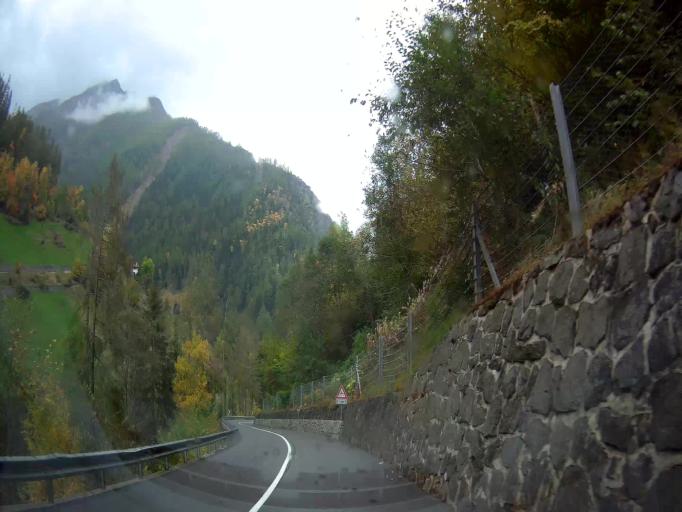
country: IT
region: Trentino-Alto Adige
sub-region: Bolzano
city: Certosa
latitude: 46.7052
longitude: 10.9145
